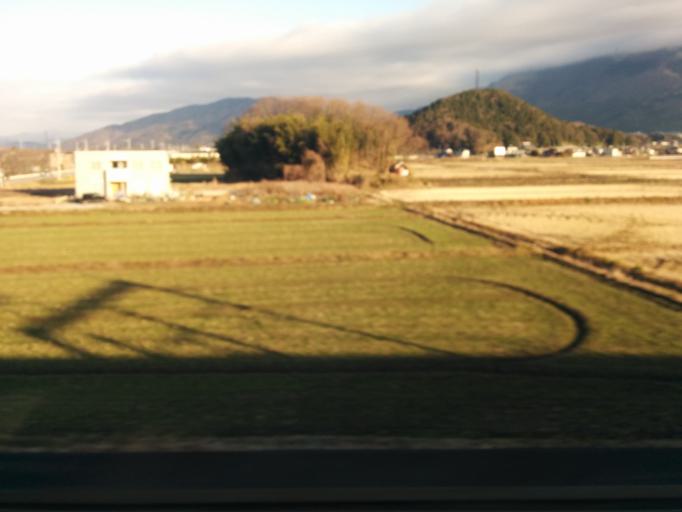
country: JP
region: Shiga Prefecture
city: Nagahama
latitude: 35.3672
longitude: 136.3697
